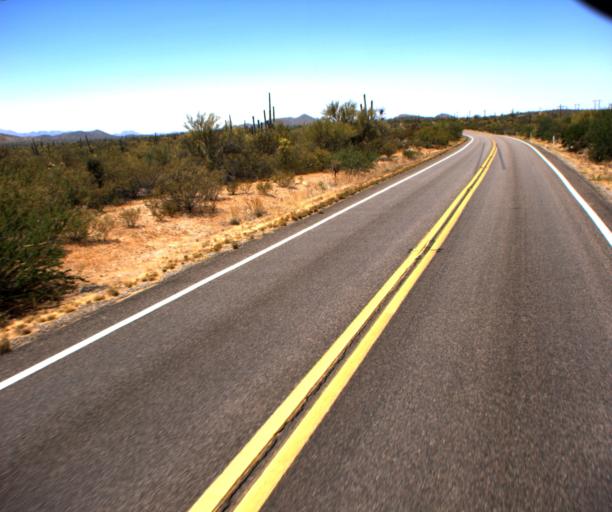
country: US
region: Arizona
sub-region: Pima County
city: Catalina
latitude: 32.6859
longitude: -111.0755
